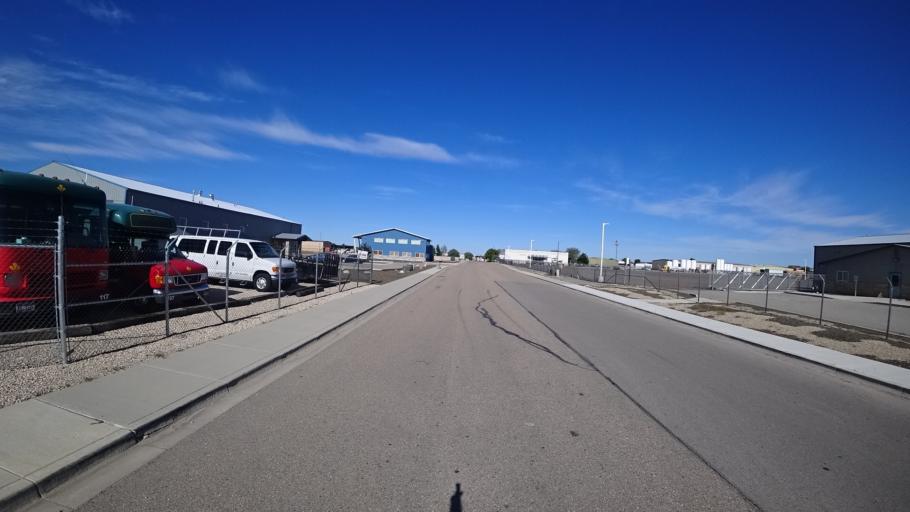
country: US
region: Idaho
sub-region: Ada County
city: Garden City
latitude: 43.5827
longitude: -116.2674
